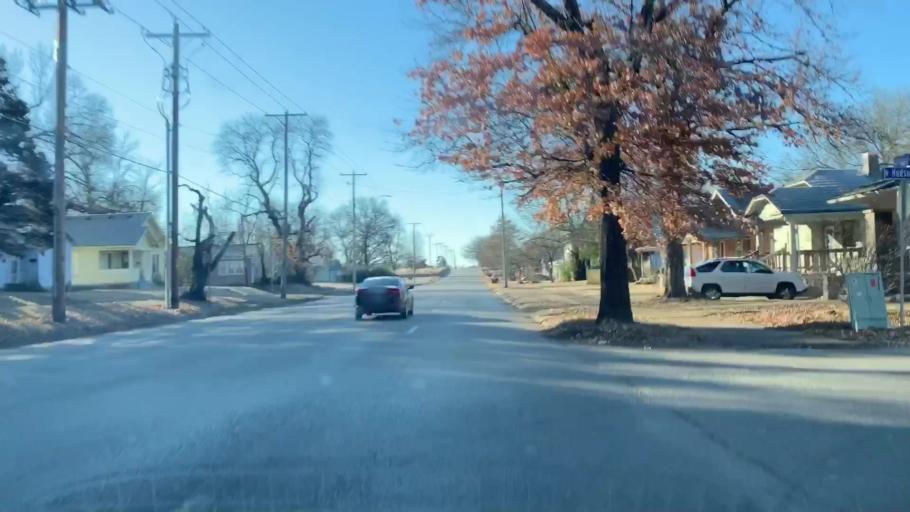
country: US
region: Kansas
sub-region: Crawford County
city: Pittsburg
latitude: 37.3880
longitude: -94.7052
